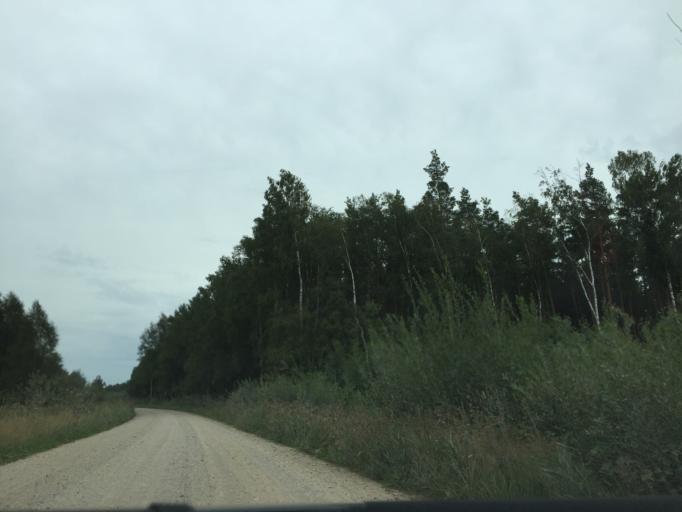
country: LV
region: Jaunpils
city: Jaunpils
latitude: 56.7291
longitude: 23.0788
